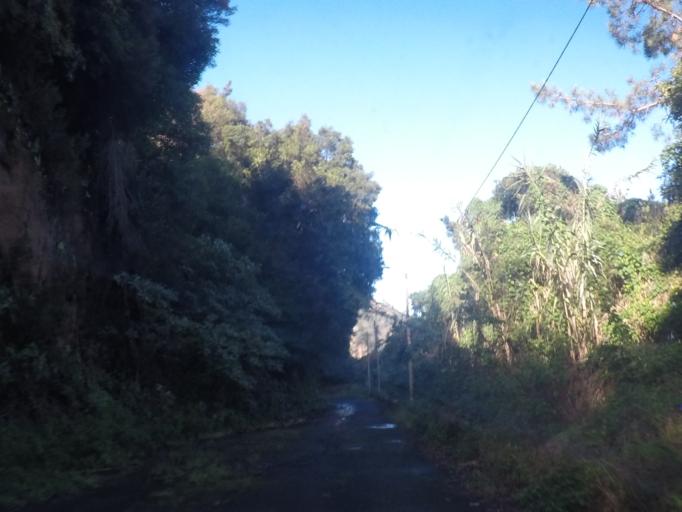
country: PT
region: Madeira
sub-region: Santana
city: Santana
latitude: 32.8181
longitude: -16.8925
